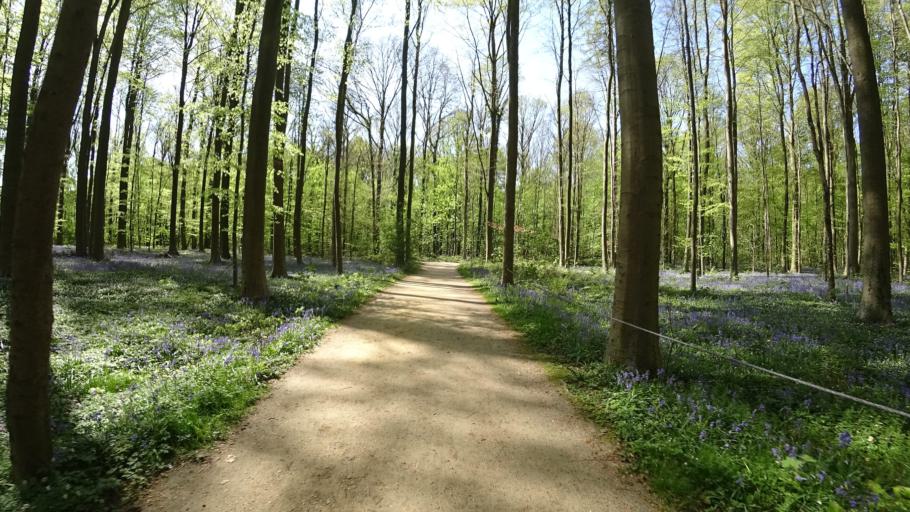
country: BE
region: Wallonia
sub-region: Province du Brabant Wallon
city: Braine-le-Chateau
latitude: 50.7007
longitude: 4.3053
